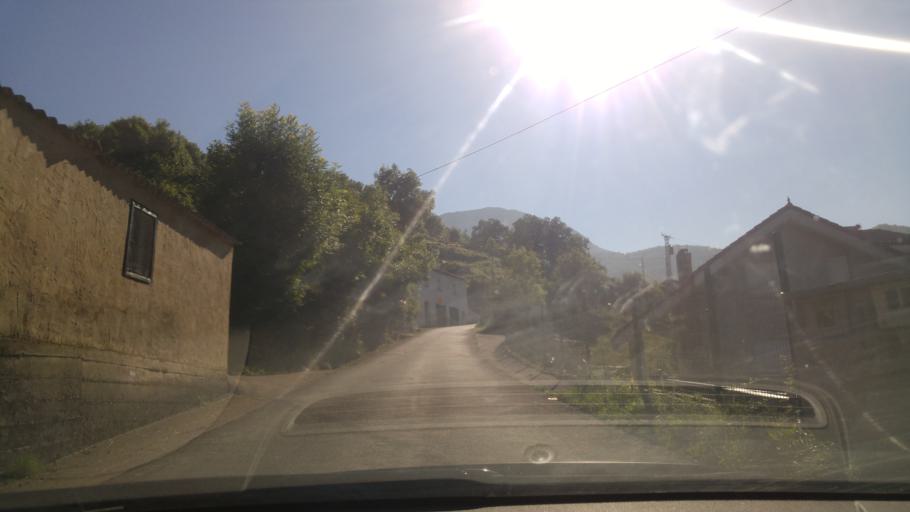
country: ES
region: Asturias
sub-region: Province of Asturias
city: Barzana
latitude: 43.1747
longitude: -5.9698
